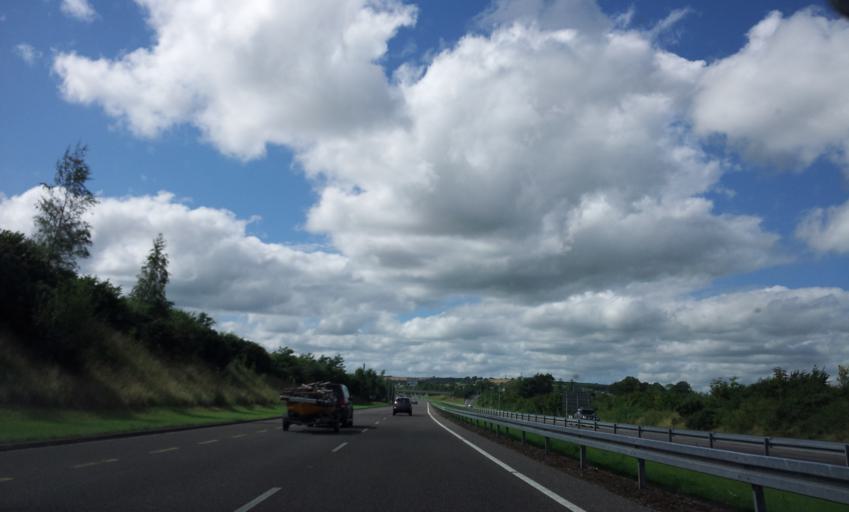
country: IE
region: Munster
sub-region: County Cork
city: Tower
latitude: 51.8747
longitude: -8.6060
